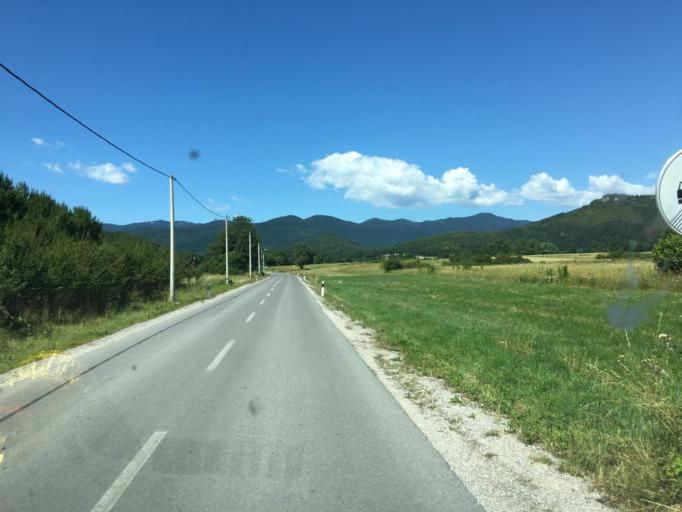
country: HR
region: Licko-Senjska
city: Gospic
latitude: 44.5616
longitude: 15.3187
